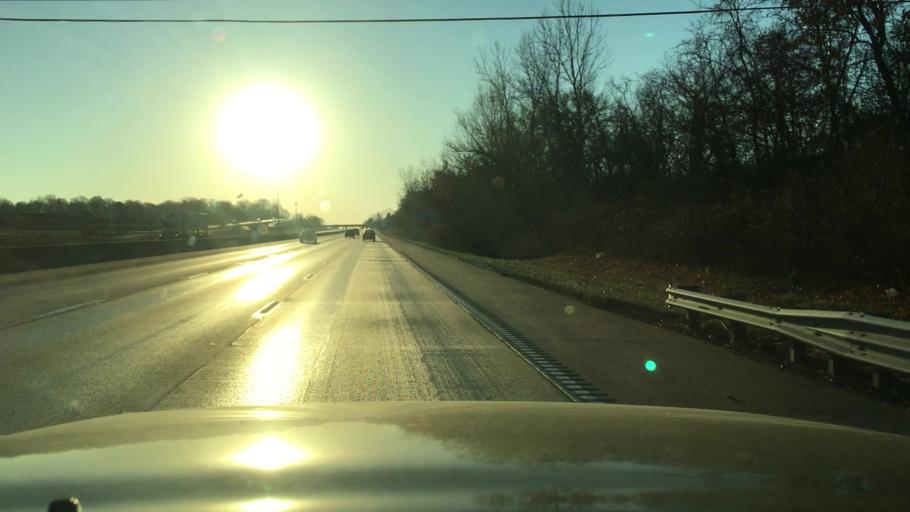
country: US
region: Missouri
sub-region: Saint Charles County
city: Saint Charles
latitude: 38.8138
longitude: -90.4914
